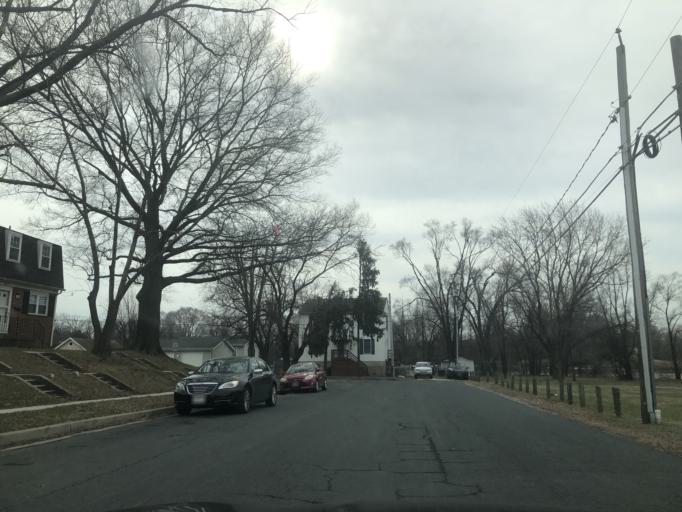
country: US
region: Maryland
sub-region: Baltimore County
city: Dundalk
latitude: 39.2621
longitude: -76.4976
